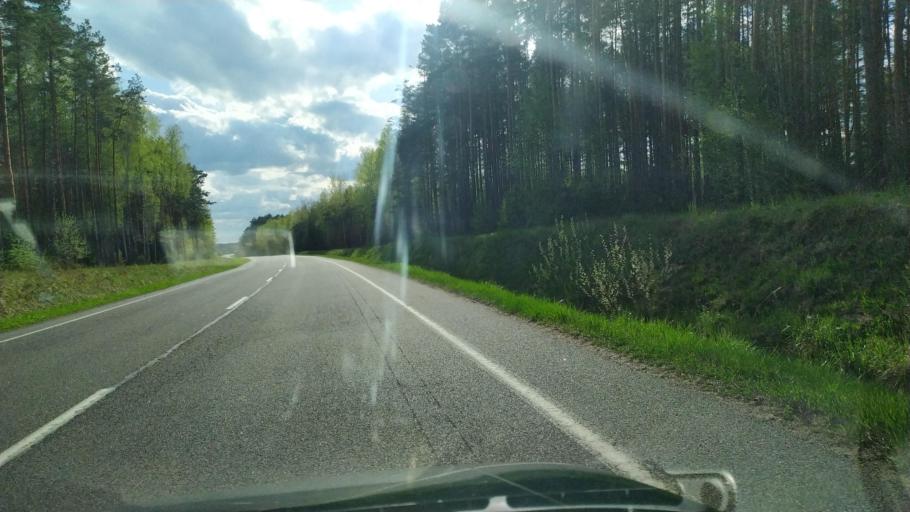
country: BY
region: Brest
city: Pruzhany
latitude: 52.7014
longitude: 24.2841
